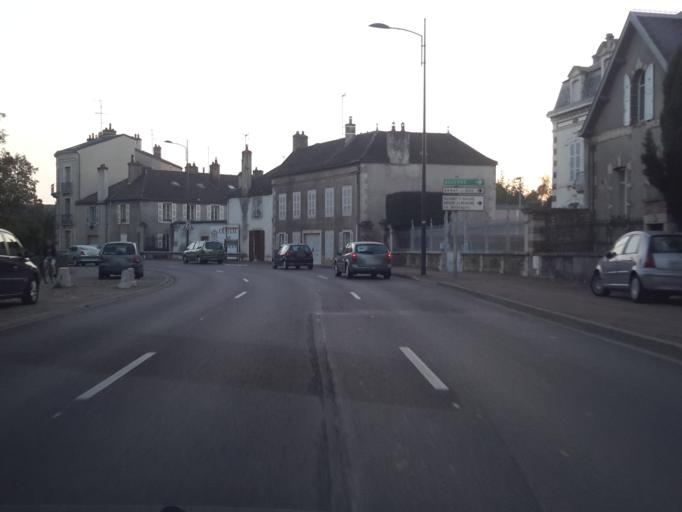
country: FR
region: Bourgogne
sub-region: Departement de la Cote-d'Or
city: Beaune
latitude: 47.0247
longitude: 4.8329
